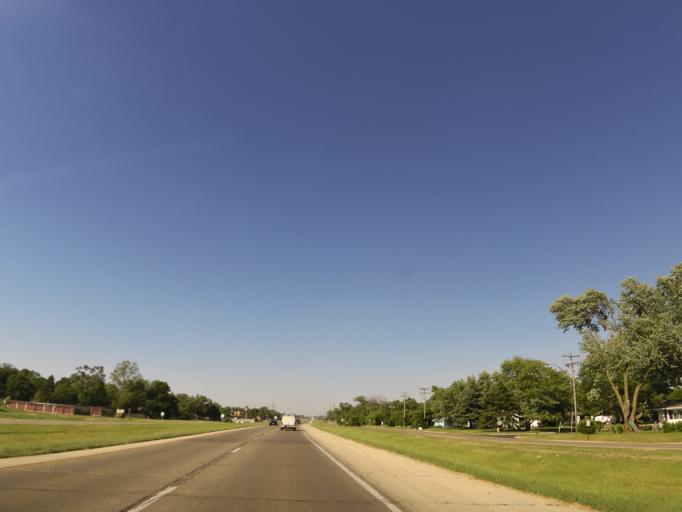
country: US
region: Illinois
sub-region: Winnebago County
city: Machesney Park
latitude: 42.3520
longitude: -89.0471
